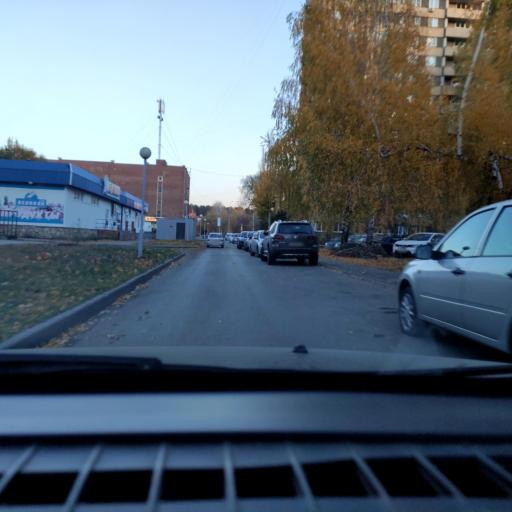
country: RU
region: Samara
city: Tol'yatti
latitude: 53.5071
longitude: 49.2986
